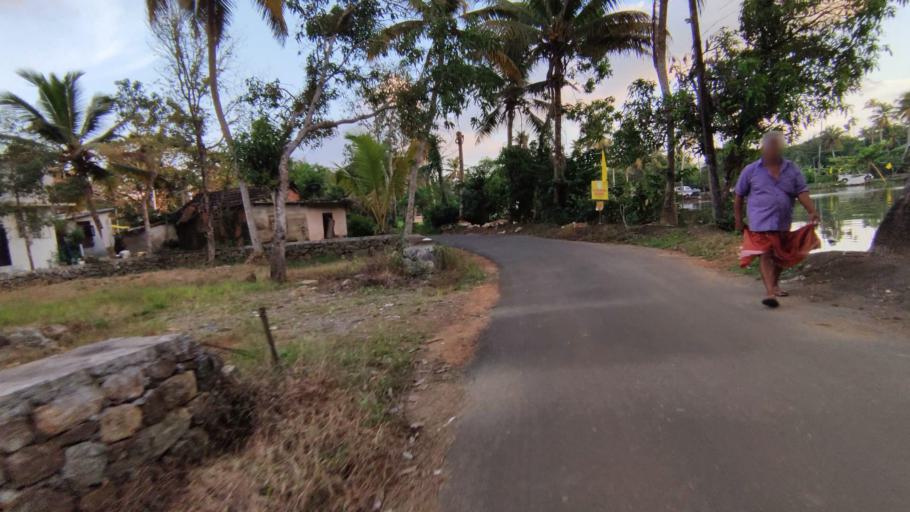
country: IN
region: Kerala
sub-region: Kottayam
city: Kottayam
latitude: 9.5771
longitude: 76.4464
